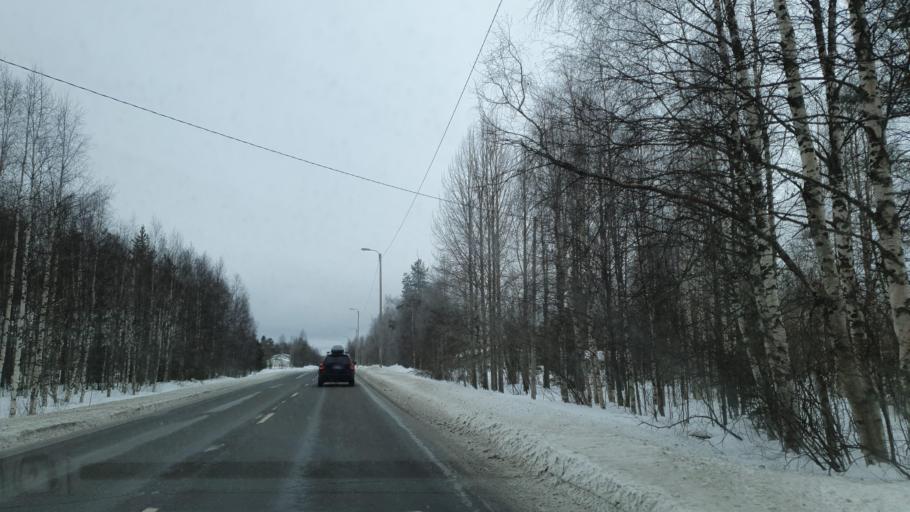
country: FI
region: Lapland
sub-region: Torniolaakso
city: Ylitornio
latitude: 66.1934
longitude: 23.8024
